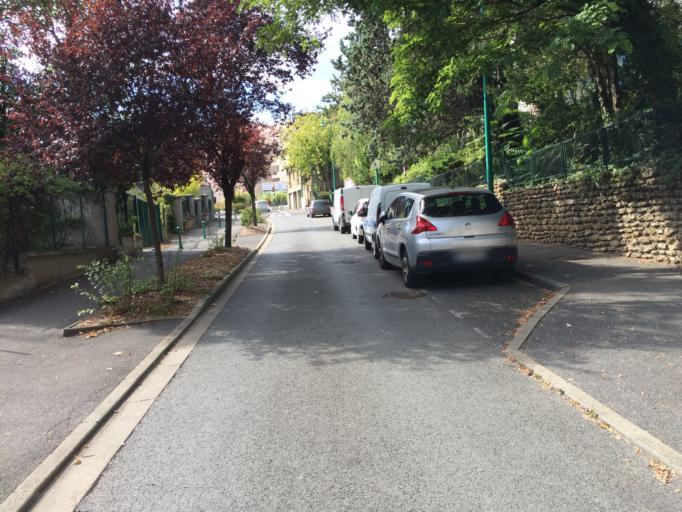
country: FR
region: Ile-de-France
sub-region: Departement de l'Essonne
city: Palaiseau
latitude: 48.7112
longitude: 2.2463
